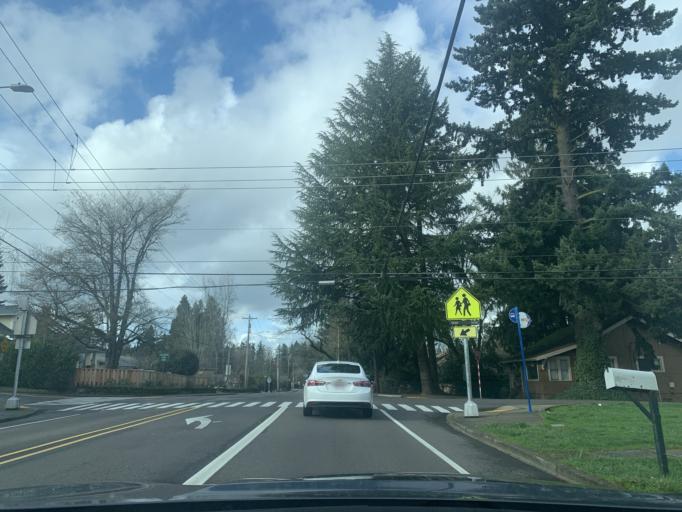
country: US
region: Oregon
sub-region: Washington County
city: Tigard
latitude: 45.4278
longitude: -122.7802
